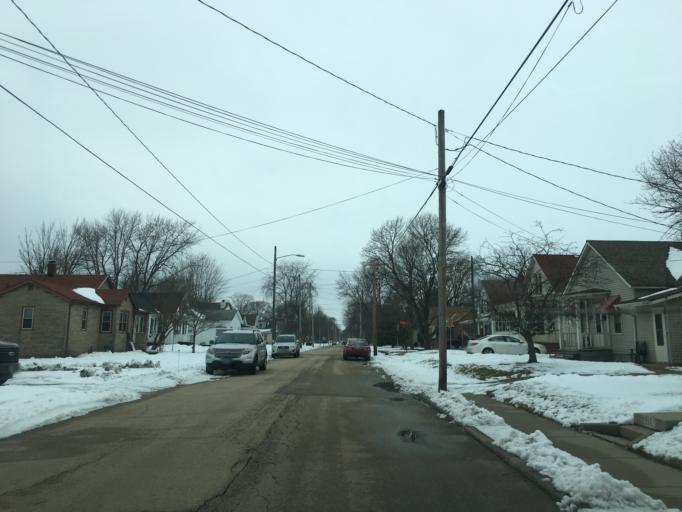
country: US
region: Illinois
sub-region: LaSalle County
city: Peru
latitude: 41.3303
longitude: -89.1365
